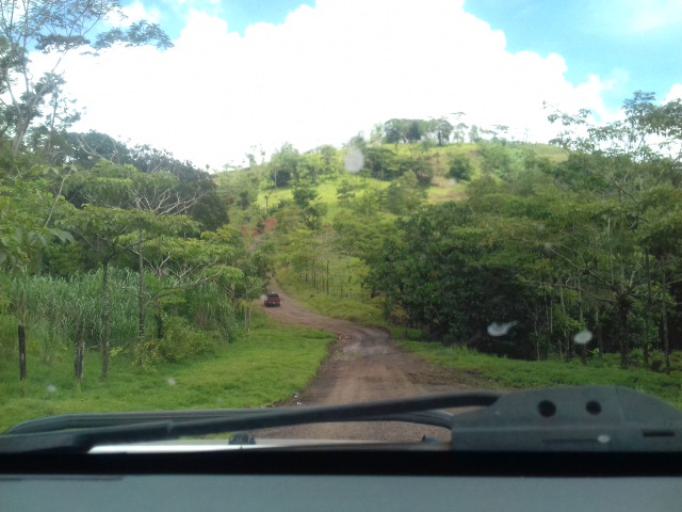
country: NI
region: Matagalpa
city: Rio Blanco
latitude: 12.9944
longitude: -85.1914
